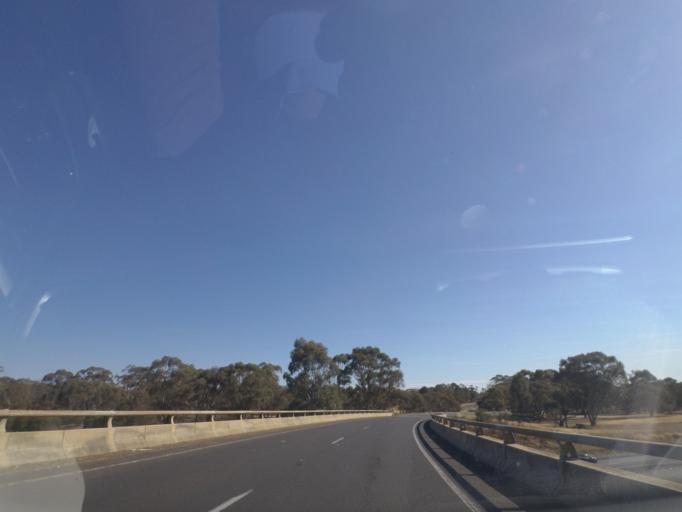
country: AU
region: Victoria
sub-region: Murrindindi
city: Kinglake West
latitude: -36.9834
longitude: 145.1459
